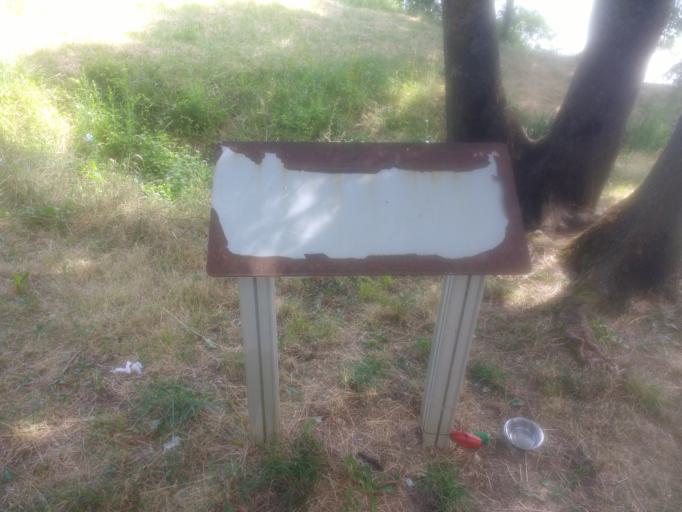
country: FR
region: Bourgogne
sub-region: Departement de Saone-et-Loire
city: Saint-Martin-Belle-Roche
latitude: 46.3583
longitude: 4.8515
